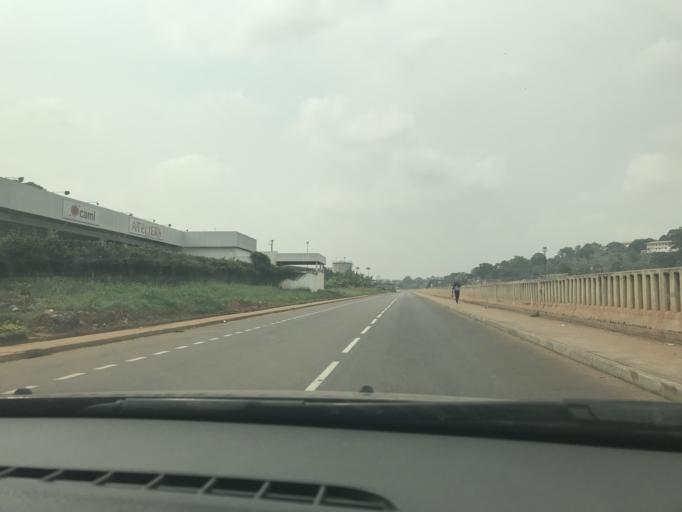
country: CM
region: Centre
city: Yaounde
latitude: 3.8467
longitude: 11.5161
